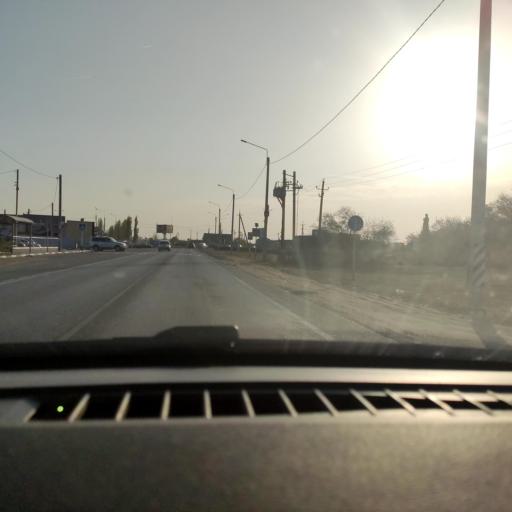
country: RU
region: Voronezj
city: Semiluki
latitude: 51.7273
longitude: 39.0364
